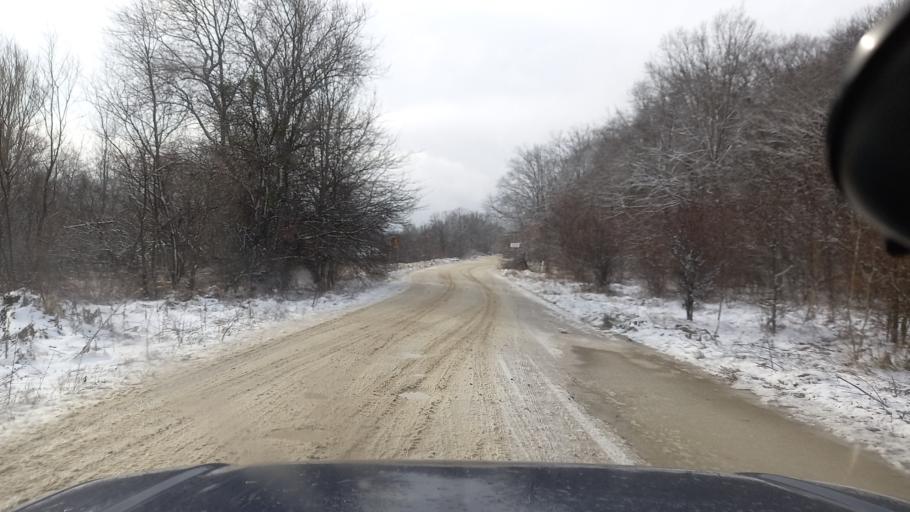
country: RU
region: Adygeya
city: Kamennomostskiy
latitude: 44.2417
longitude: 40.1978
